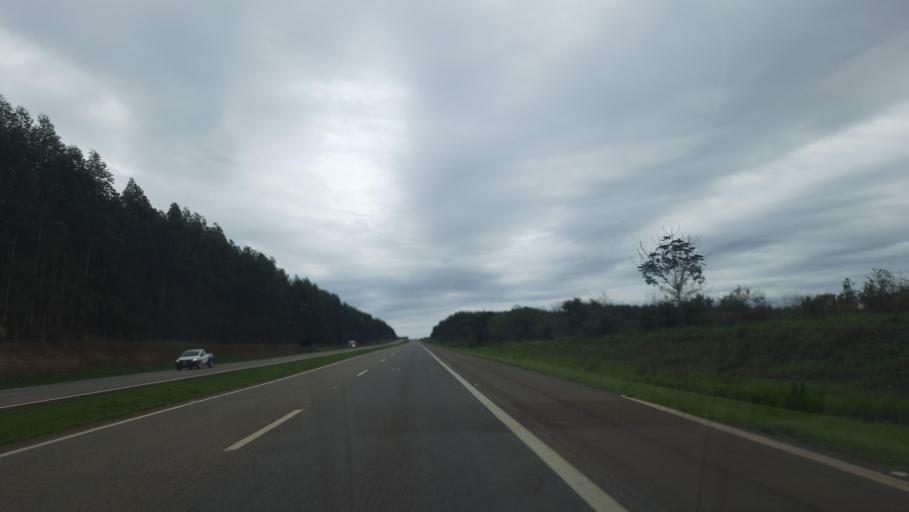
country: BR
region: Sao Paulo
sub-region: Casa Branca
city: Casa Branca
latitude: -21.8606
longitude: -47.0625
